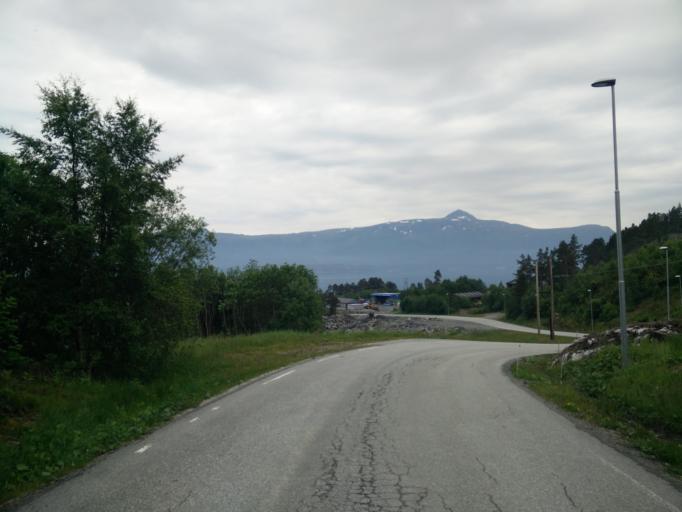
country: NO
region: More og Romsdal
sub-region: Kristiansund
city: Rensvik
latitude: 63.0146
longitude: 7.9698
